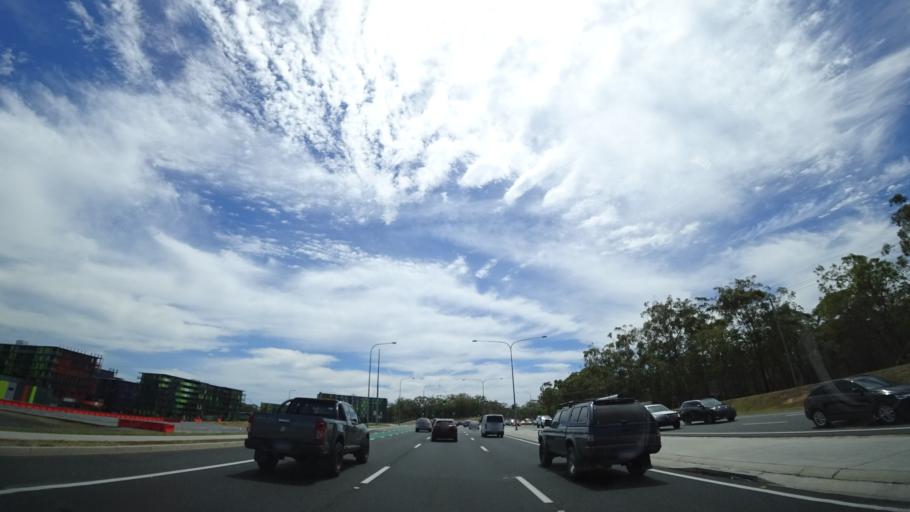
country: AU
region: Queensland
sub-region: Gold Coast
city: Southport
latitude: -27.9637
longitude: 153.3880
